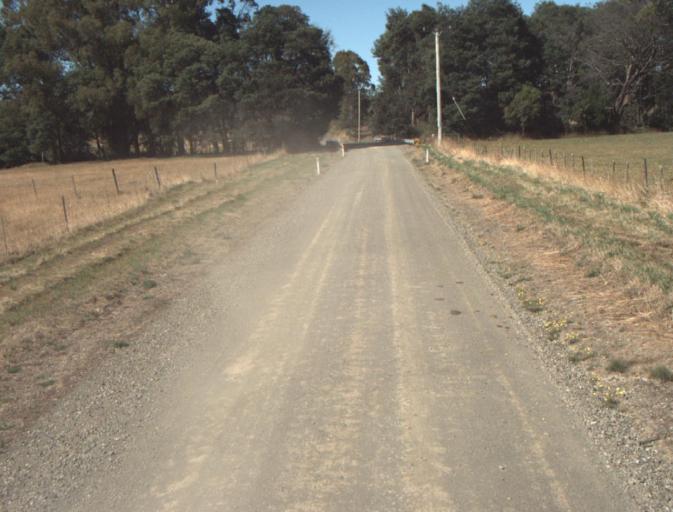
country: AU
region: Tasmania
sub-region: Launceston
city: Newstead
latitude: -41.3166
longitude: 147.3201
